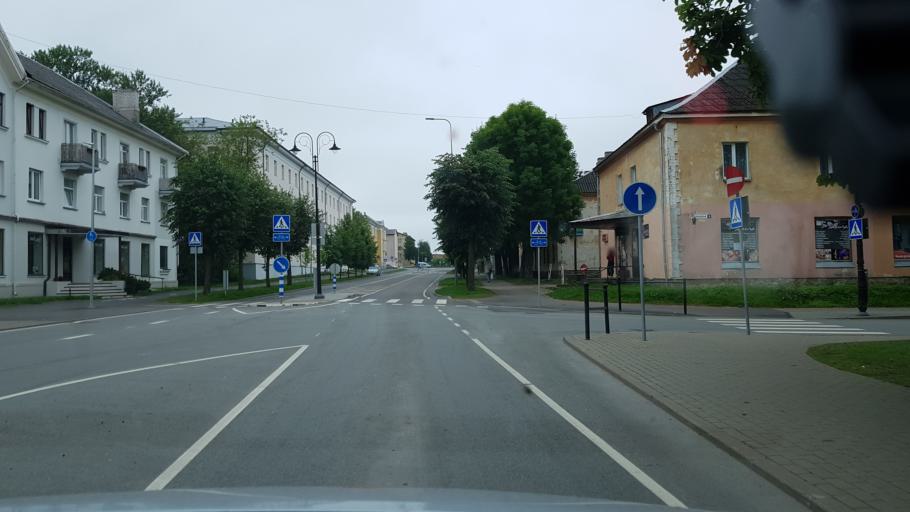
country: EE
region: Ida-Virumaa
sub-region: Kohtla-Jaerve linn
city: Kohtla-Jarve
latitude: 59.4025
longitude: 27.2870
